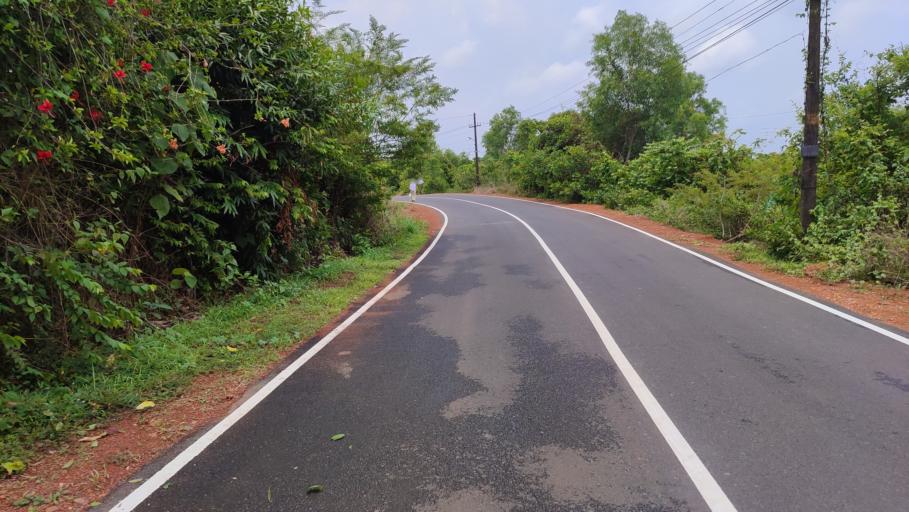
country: IN
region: Kerala
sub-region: Kasaragod District
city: Kannangad
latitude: 12.3162
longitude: 75.1431
